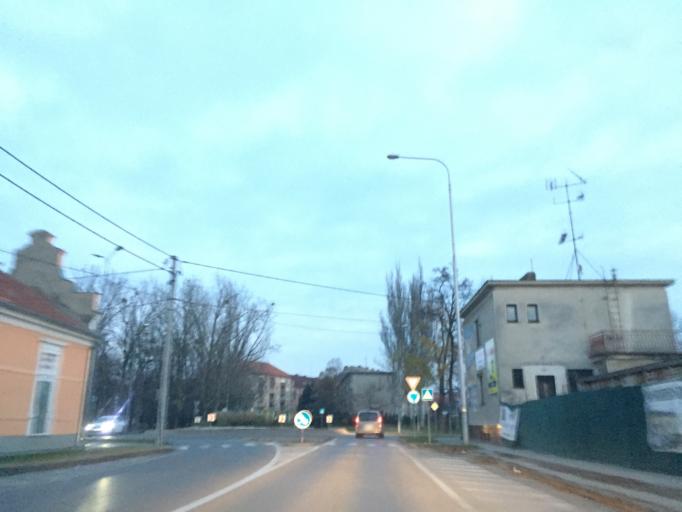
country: SK
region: Nitriansky
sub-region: Okres Nove Zamky
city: Nove Zamky
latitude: 47.9884
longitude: 18.1565
